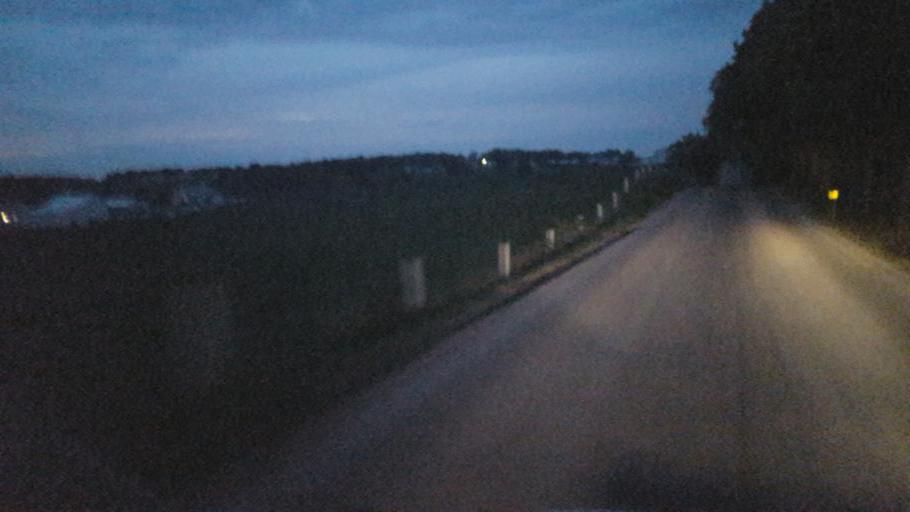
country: US
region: Ohio
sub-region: Wayne County
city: Apple Creek
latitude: 40.6576
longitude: -81.7747
